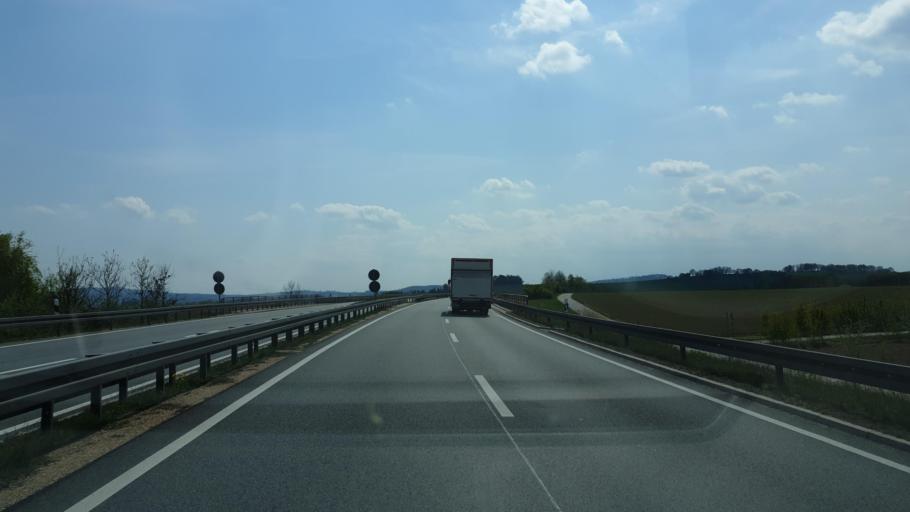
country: DE
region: Saxony
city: Lobau
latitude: 51.1047
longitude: 14.6487
